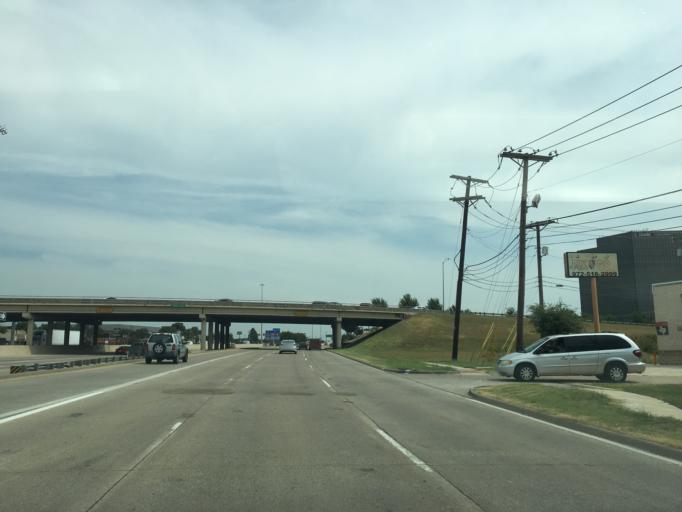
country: US
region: Texas
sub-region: Collin County
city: Plano
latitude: 33.0275
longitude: -96.7090
